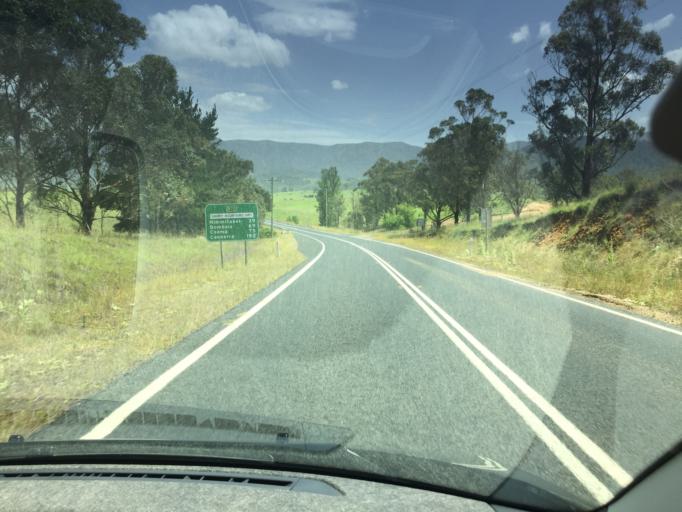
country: AU
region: New South Wales
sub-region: Bega Valley
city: Bega
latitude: -36.6223
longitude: 149.5618
